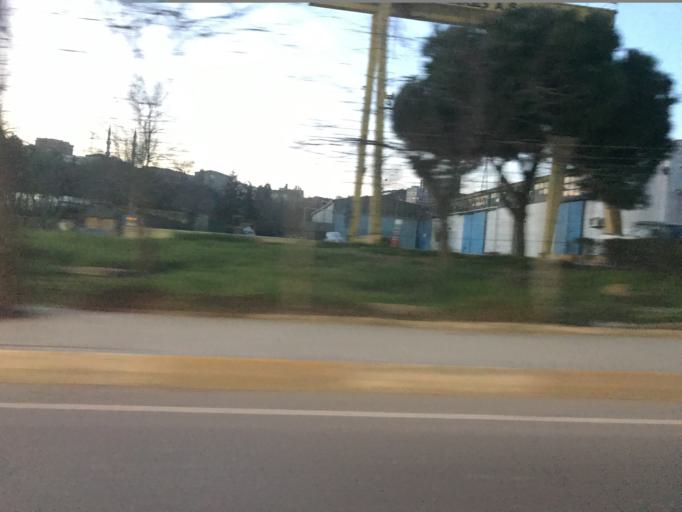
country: TR
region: Istanbul
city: Pendik
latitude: 40.8997
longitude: 29.2718
